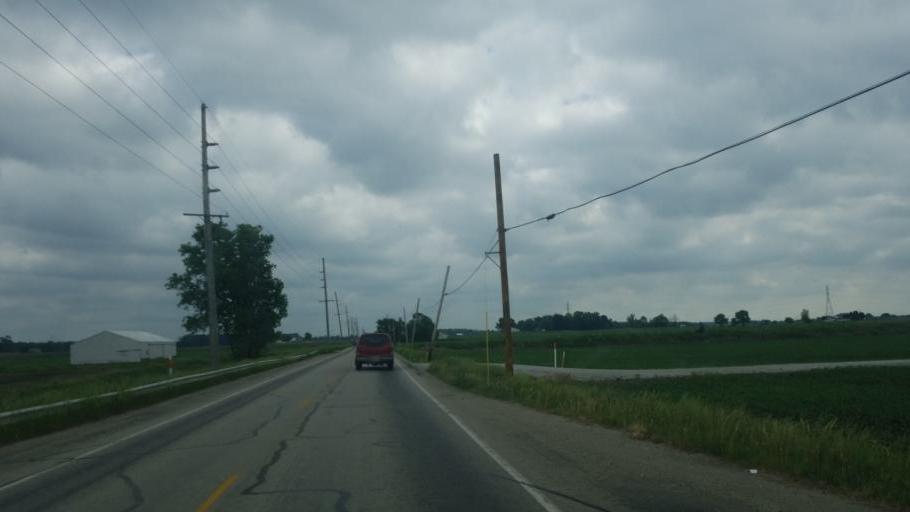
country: US
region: Indiana
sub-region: Elkhart County
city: Nappanee
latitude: 41.4132
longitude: -86.0012
